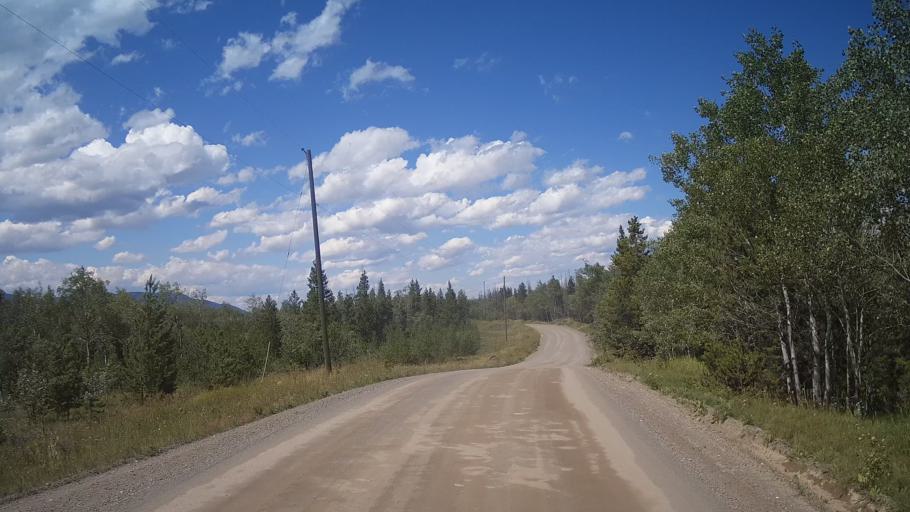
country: CA
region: British Columbia
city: Cache Creek
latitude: 51.2482
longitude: -121.6627
